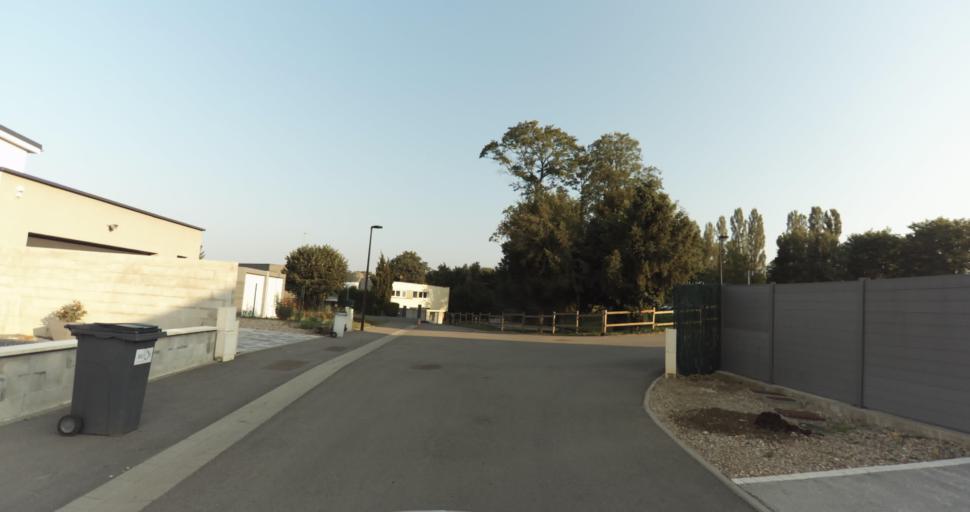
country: FR
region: Lorraine
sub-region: Departement de Meurthe-et-Moselle
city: Briey
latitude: 49.2454
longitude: 5.9418
